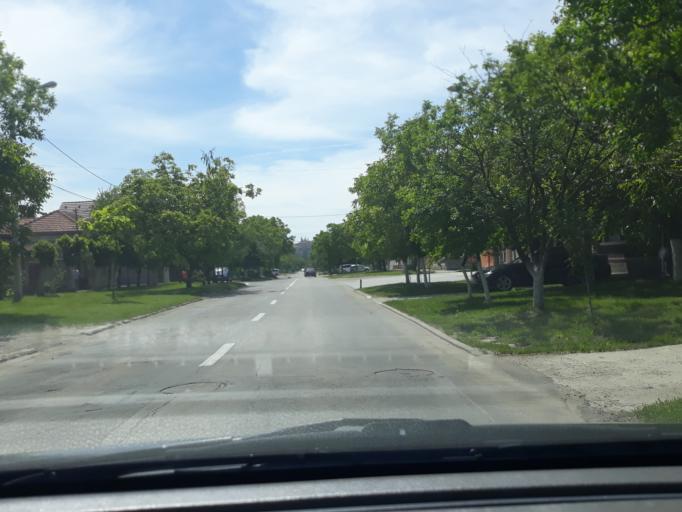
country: RO
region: Bihor
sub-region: Comuna Biharea
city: Oradea
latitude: 47.0609
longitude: 21.9058
